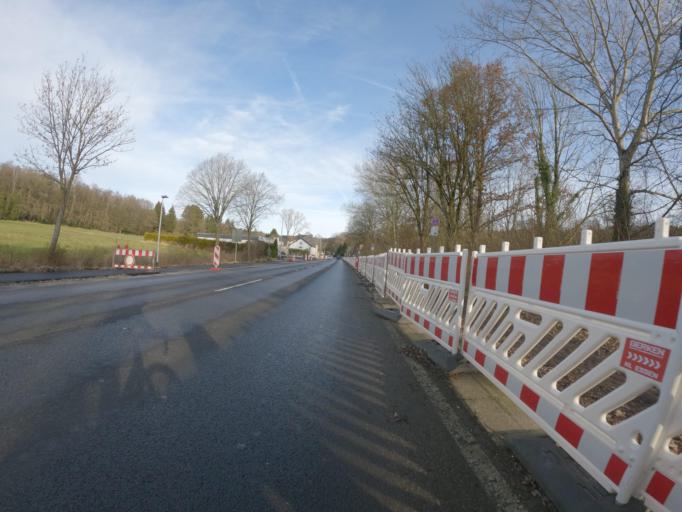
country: BE
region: Wallonia
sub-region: Province de Liege
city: La Calamine
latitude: 50.7292
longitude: 6.0385
